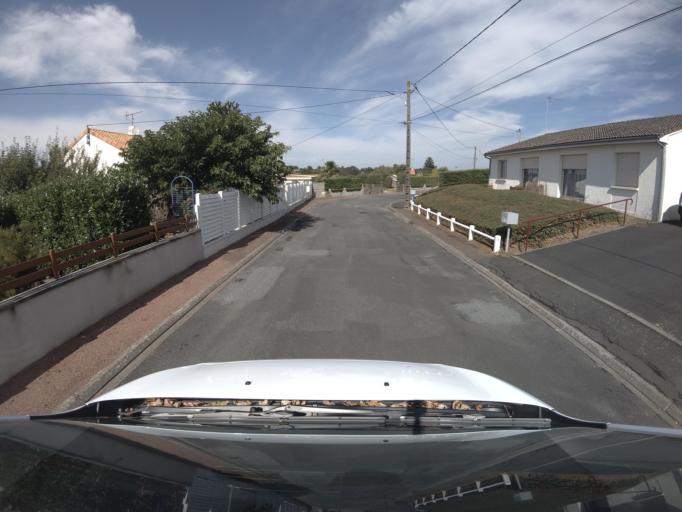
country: FR
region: Poitou-Charentes
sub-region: Departement des Deux-Sevres
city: Argenton-les-Vallees
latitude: 46.9878
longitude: -0.4537
